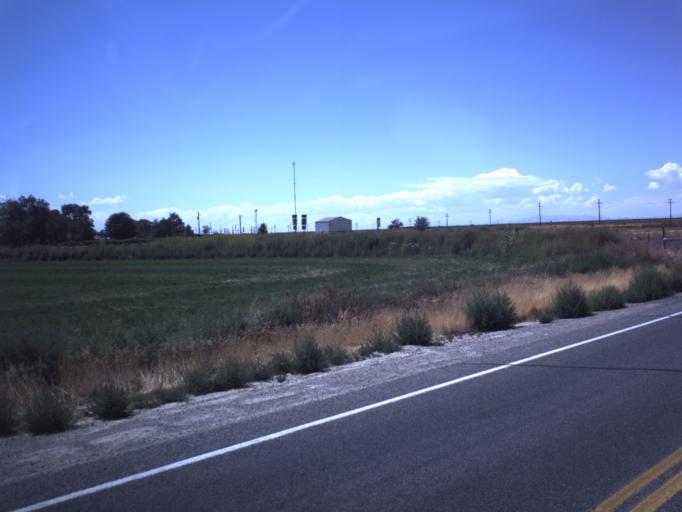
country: US
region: Utah
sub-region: Millard County
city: Delta
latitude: 39.5246
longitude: -112.3712
